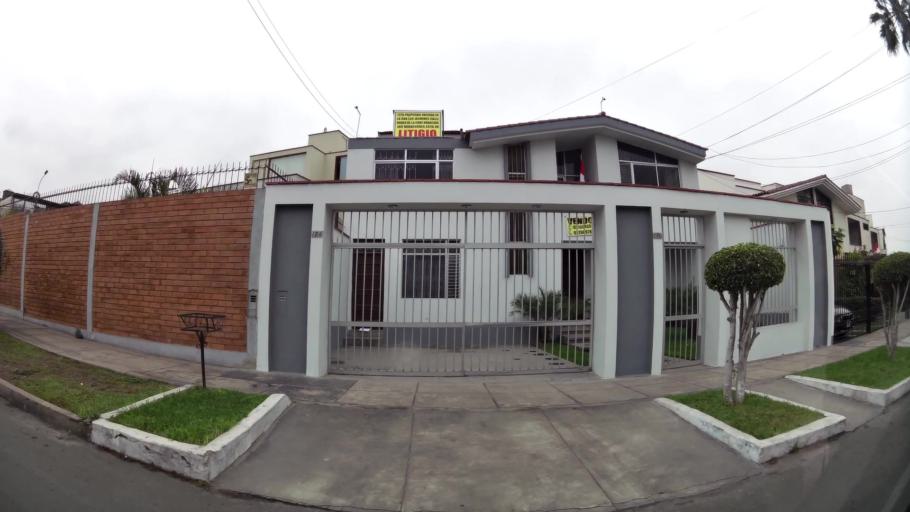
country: PE
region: Lima
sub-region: Lima
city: Surco
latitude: -12.1260
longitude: -77.0065
